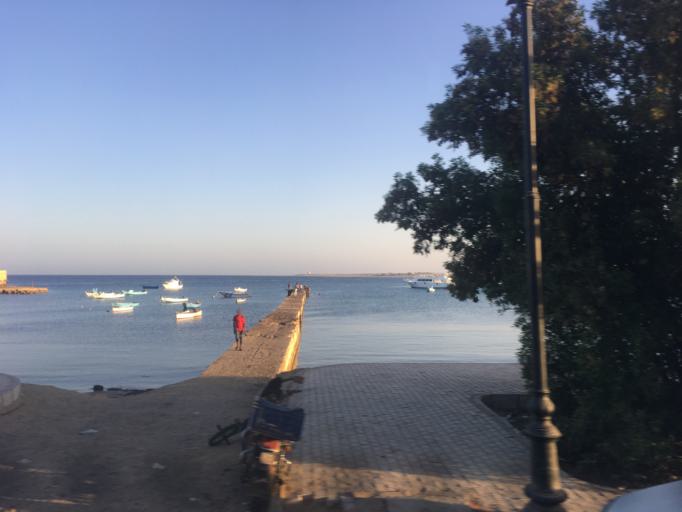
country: EG
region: Red Sea
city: Al Qusayr
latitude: 26.1033
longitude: 34.2852
